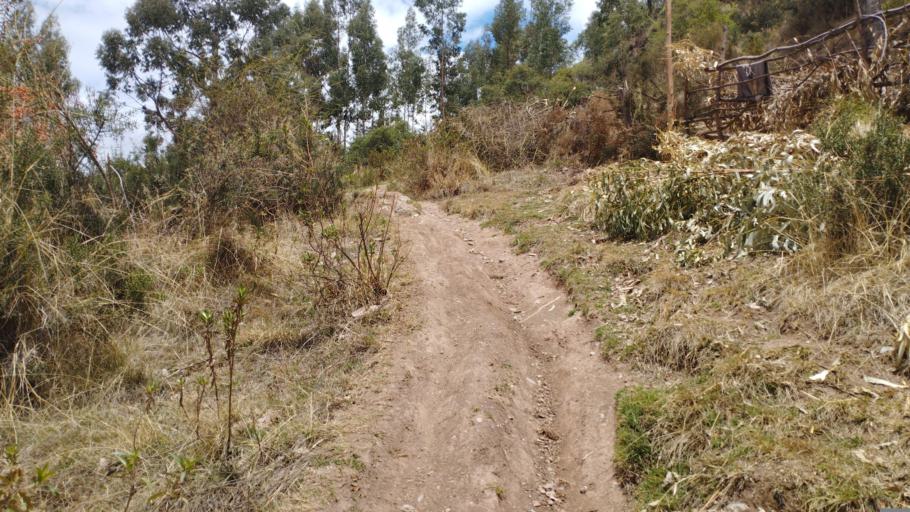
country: PE
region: Cusco
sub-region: Provincia de Cusco
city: Cusco
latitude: -13.5198
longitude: -71.9457
